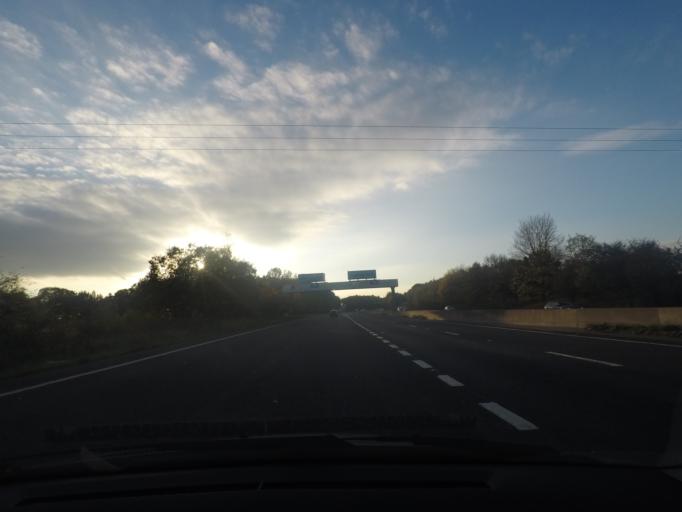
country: GB
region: England
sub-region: North Lincolnshire
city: Scawby
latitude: 53.5444
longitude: -0.5493
